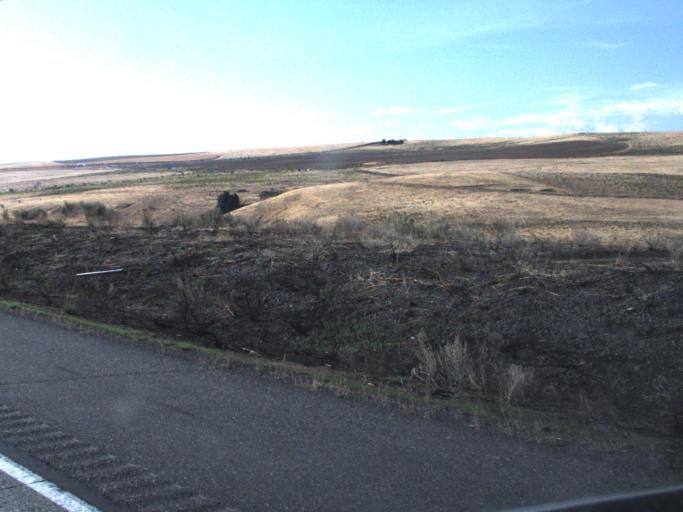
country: US
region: Oregon
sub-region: Umatilla County
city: Umatilla
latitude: 45.9842
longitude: -119.3126
